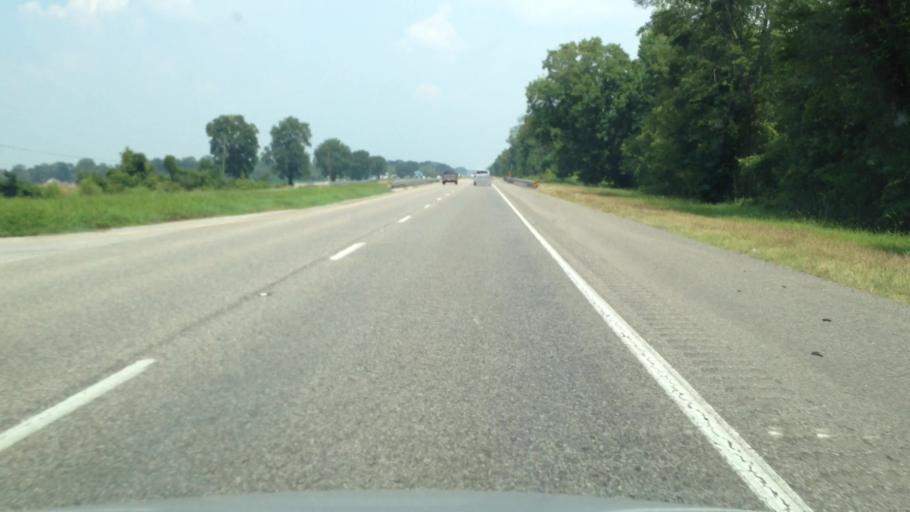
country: US
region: Louisiana
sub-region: West Baton Rouge Parish
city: Erwinville
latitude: 30.5220
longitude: -91.3748
